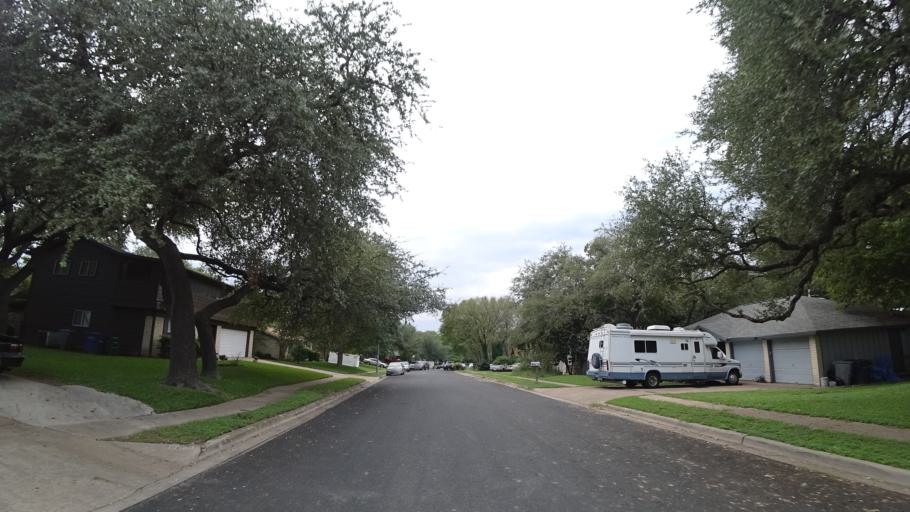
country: US
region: Texas
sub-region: Travis County
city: Onion Creek
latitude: 30.2021
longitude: -97.7808
